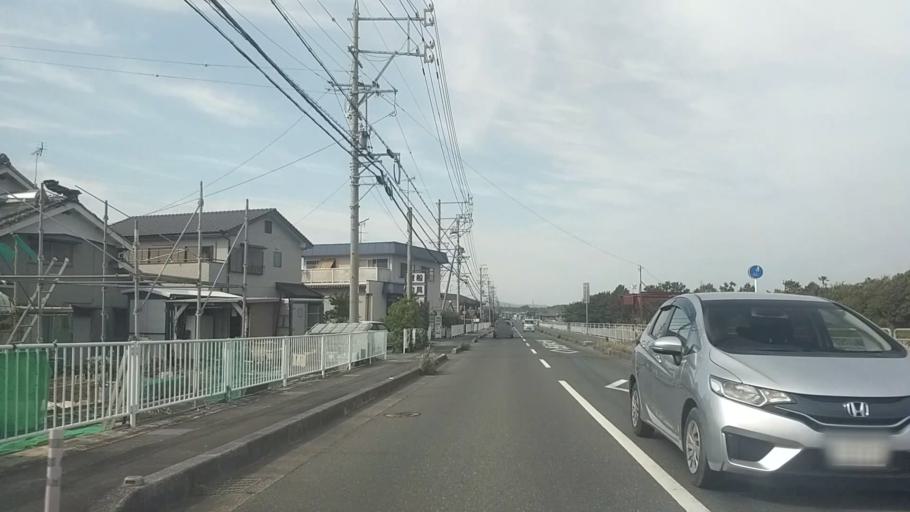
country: JP
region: Shizuoka
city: Kosai-shi
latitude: 34.7165
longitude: 137.5914
